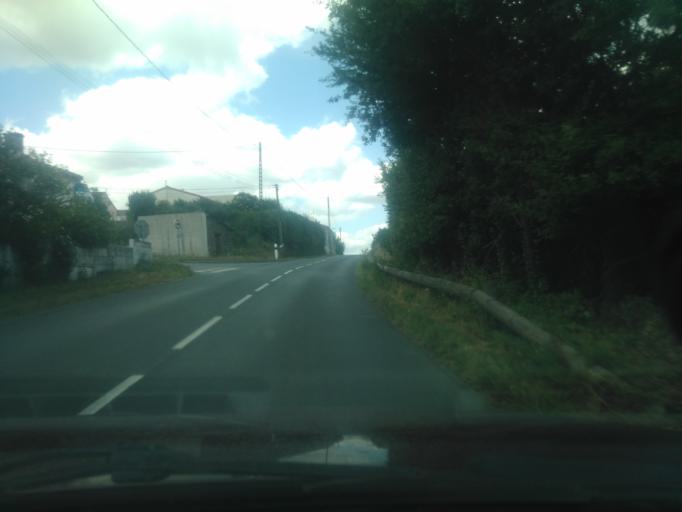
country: FR
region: Pays de la Loire
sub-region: Departement de la Vendee
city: Chauche
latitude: 46.8201
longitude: -1.2666
